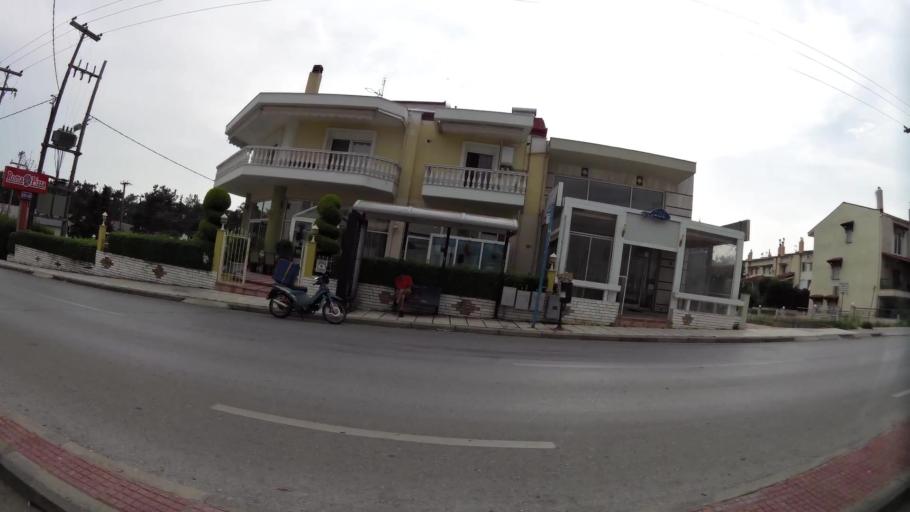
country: GR
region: Central Macedonia
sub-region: Nomos Thessalonikis
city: Oraiokastro
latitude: 40.7226
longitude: 22.9249
